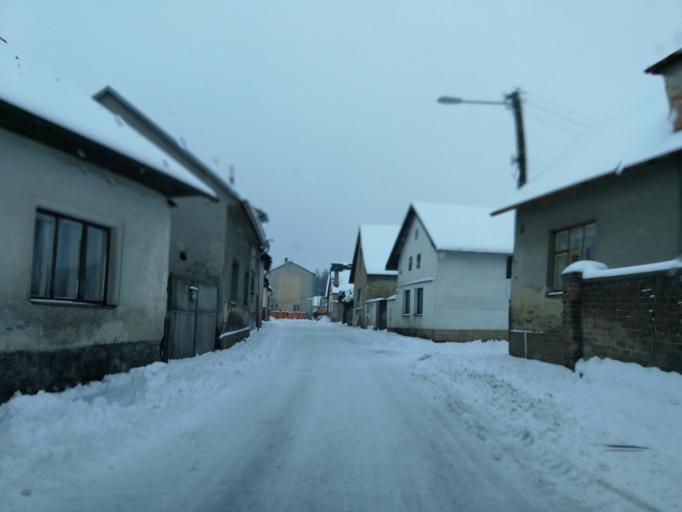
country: CZ
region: Vysocina
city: Heralec
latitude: 49.5298
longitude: 15.4594
